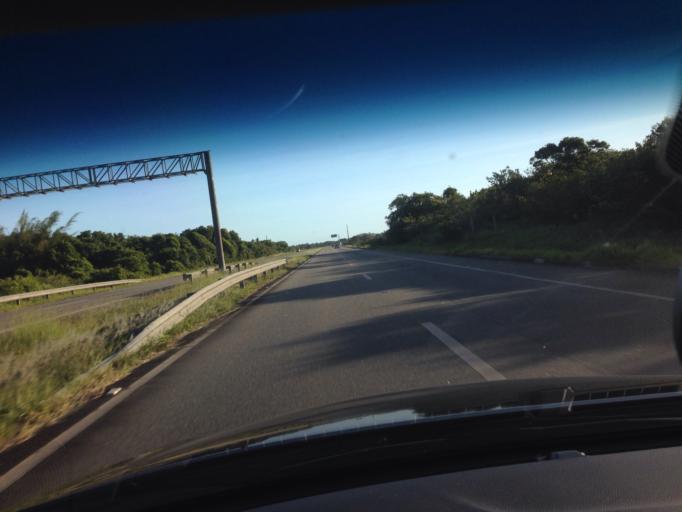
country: BR
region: Espirito Santo
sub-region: Guarapari
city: Guarapari
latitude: -20.5995
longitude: -40.4261
